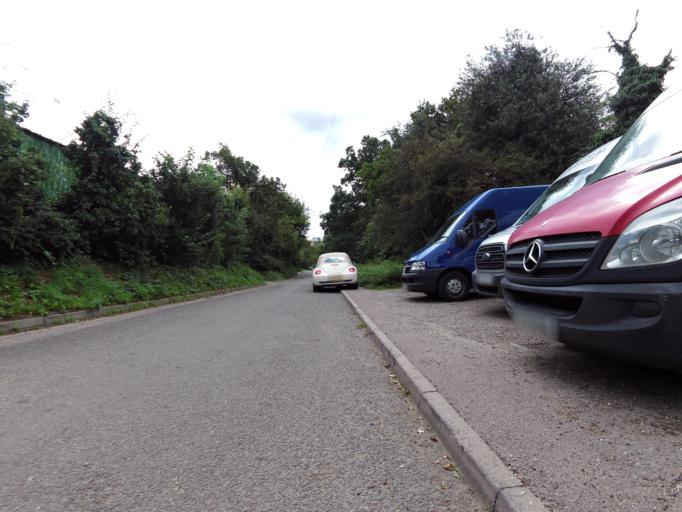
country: GB
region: England
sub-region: Hertfordshire
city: Hatfield
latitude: 51.7402
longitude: -0.2664
